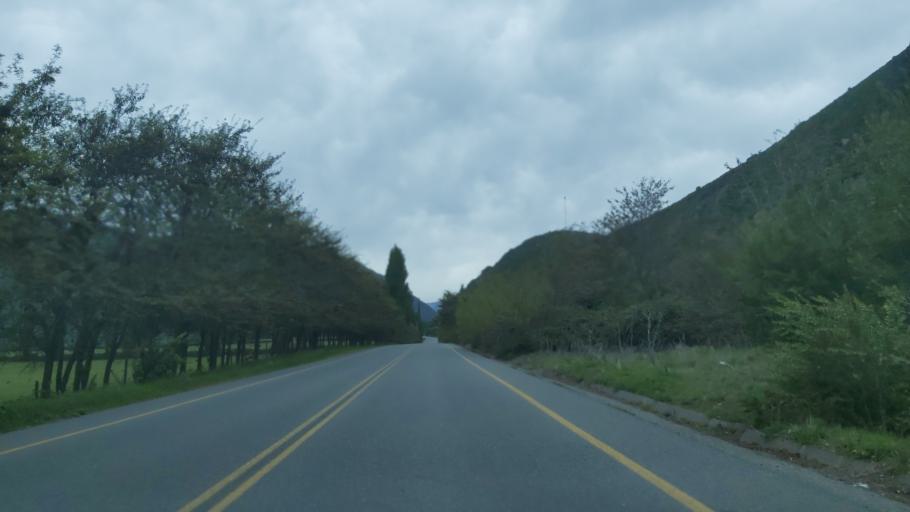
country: CL
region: Maule
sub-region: Provincia de Linares
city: Colbun
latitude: -35.8127
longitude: -70.8621
